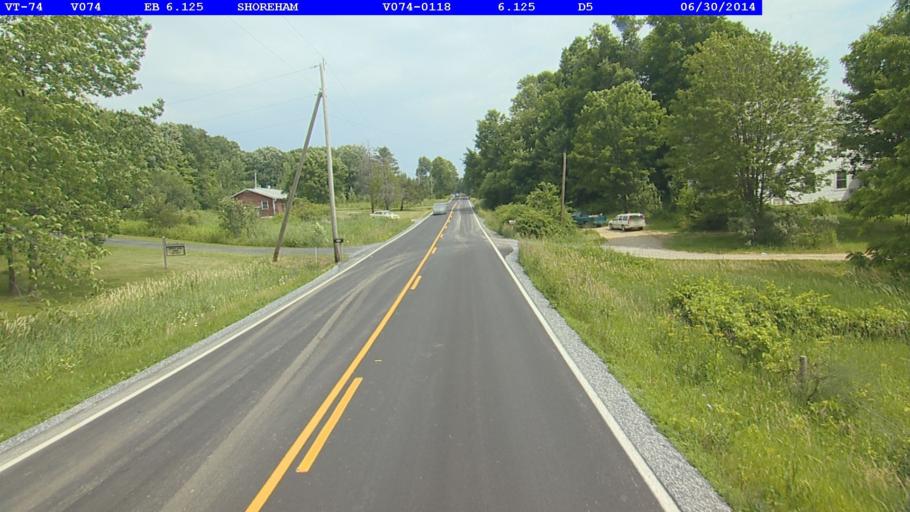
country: US
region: New York
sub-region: Essex County
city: Ticonderoga
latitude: 43.9081
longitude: -73.2972
